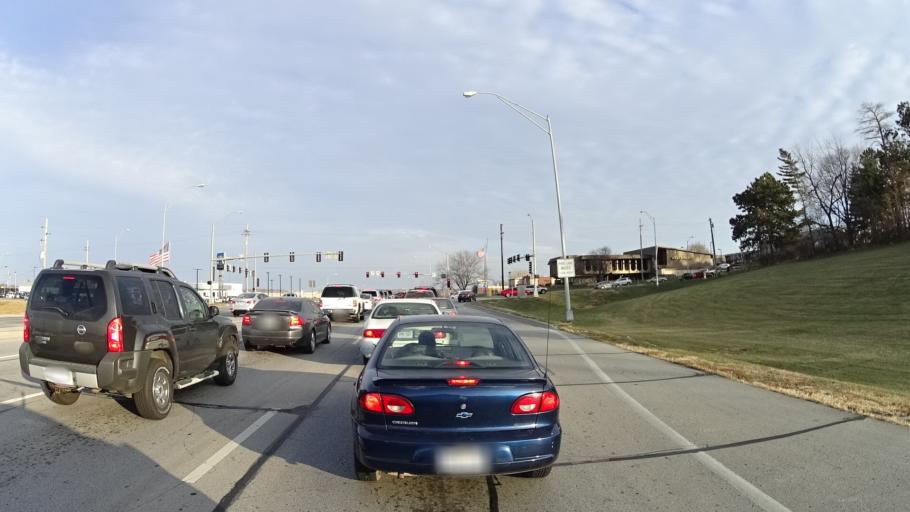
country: US
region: Nebraska
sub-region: Douglas County
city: Ralston
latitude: 41.2124
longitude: -96.0442
